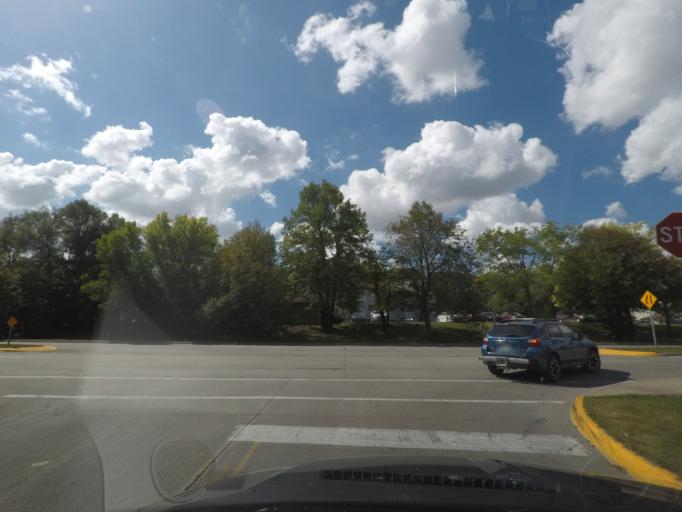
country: US
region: Iowa
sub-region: Story County
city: Ames
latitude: 42.0115
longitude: -93.6466
